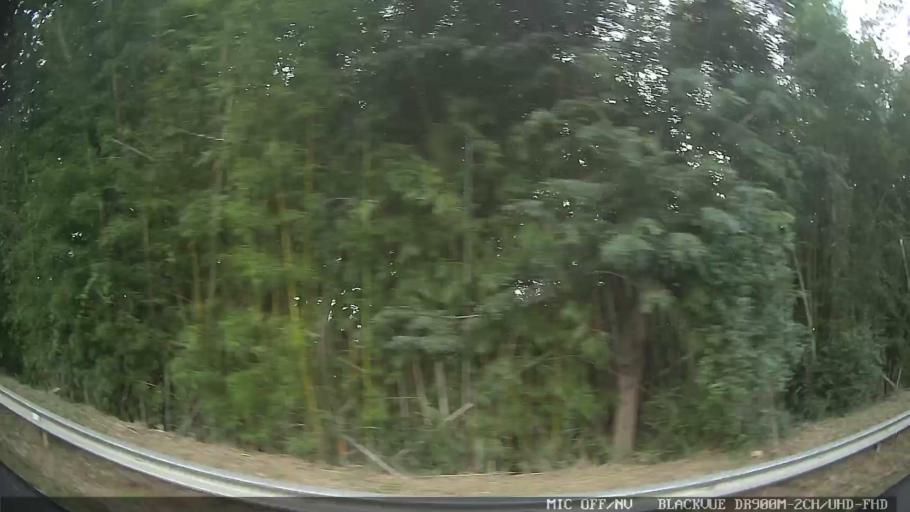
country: BR
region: Sao Paulo
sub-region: Porto Feliz
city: Porto Feliz
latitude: -23.2040
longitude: -47.6016
